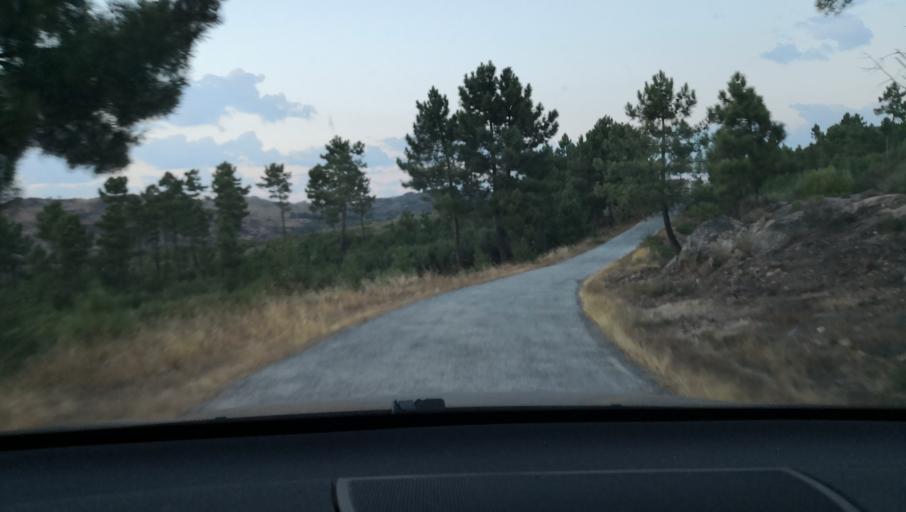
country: PT
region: Vila Real
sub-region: Sabrosa
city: Sabrosa
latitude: 41.2752
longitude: -7.6268
